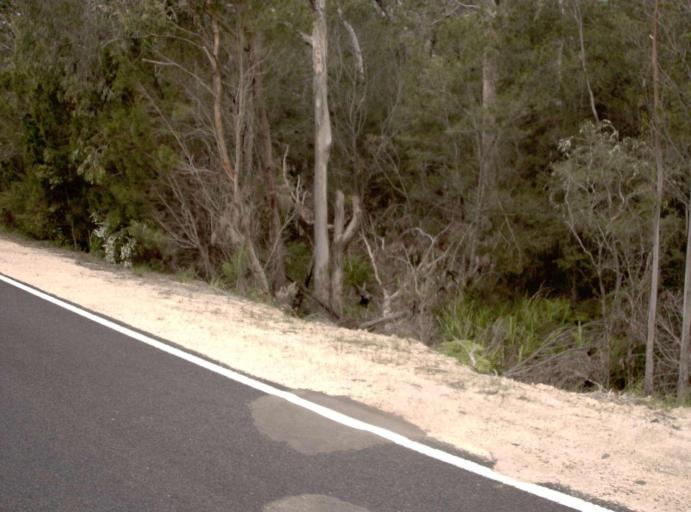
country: AU
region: New South Wales
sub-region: Bega Valley
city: Eden
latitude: -37.4072
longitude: 149.6608
